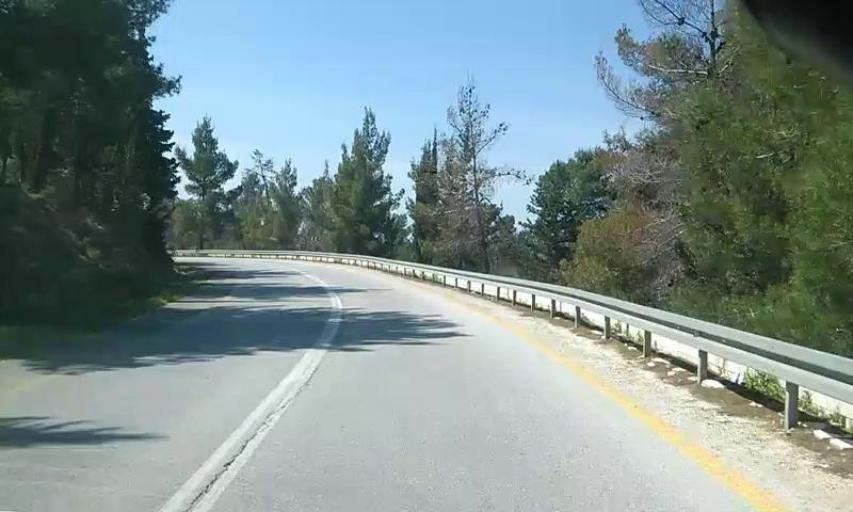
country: PS
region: West Bank
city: Nahhalin
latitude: 31.6751
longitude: 35.0952
